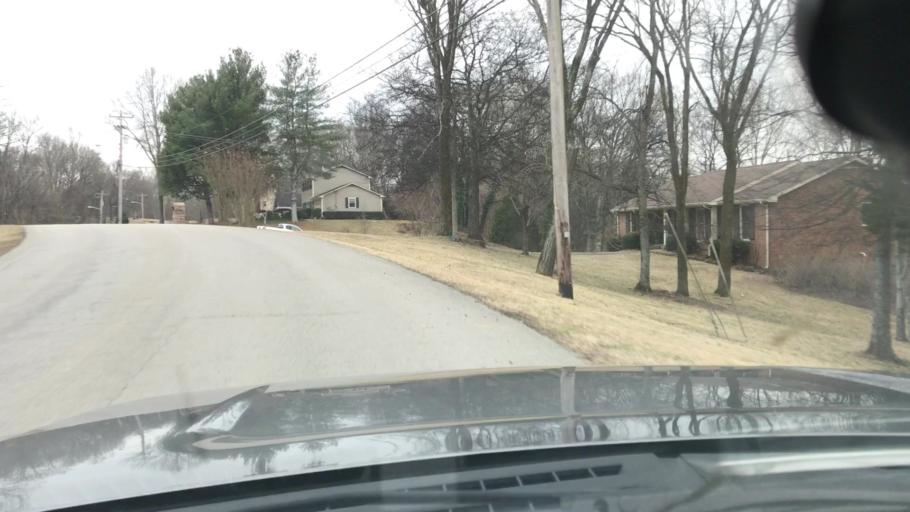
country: US
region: Tennessee
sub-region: Williamson County
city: Brentwood Estates
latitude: 36.0081
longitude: -86.7203
